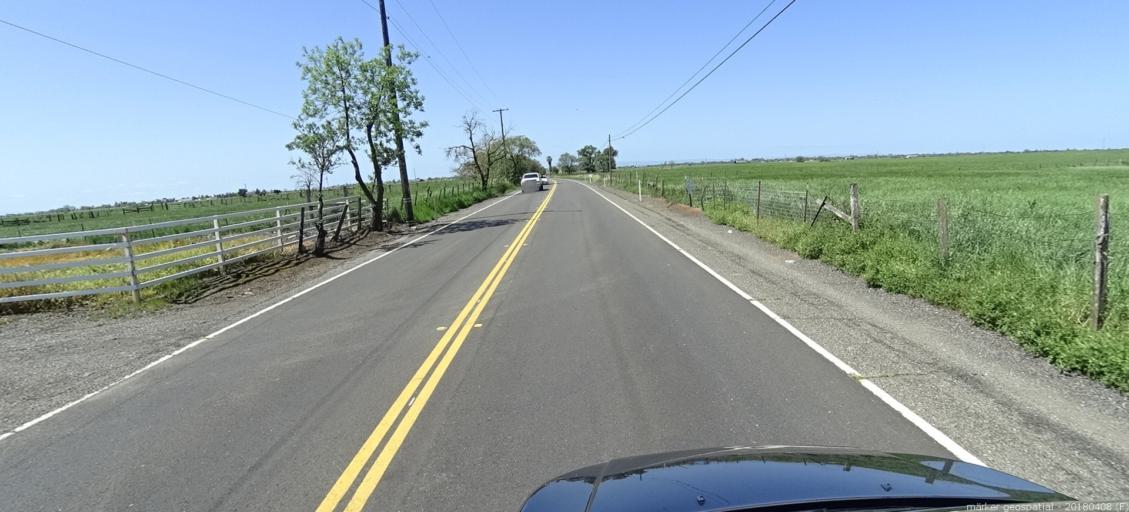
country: US
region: California
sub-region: Sacramento County
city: Laguna
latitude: 38.3760
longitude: -121.4672
